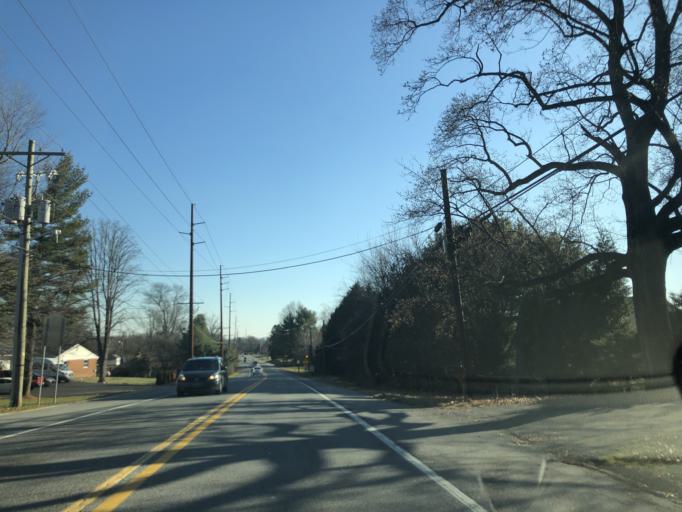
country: US
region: Delaware
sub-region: New Castle County
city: Hockessin
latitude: 39.7716
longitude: -75.6706
